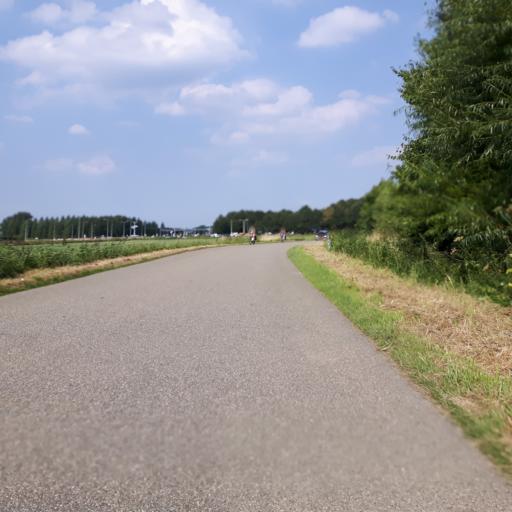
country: NL
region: Zeeland
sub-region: Gemeente Goes
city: Goes
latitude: 51.4713
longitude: 3.9345
